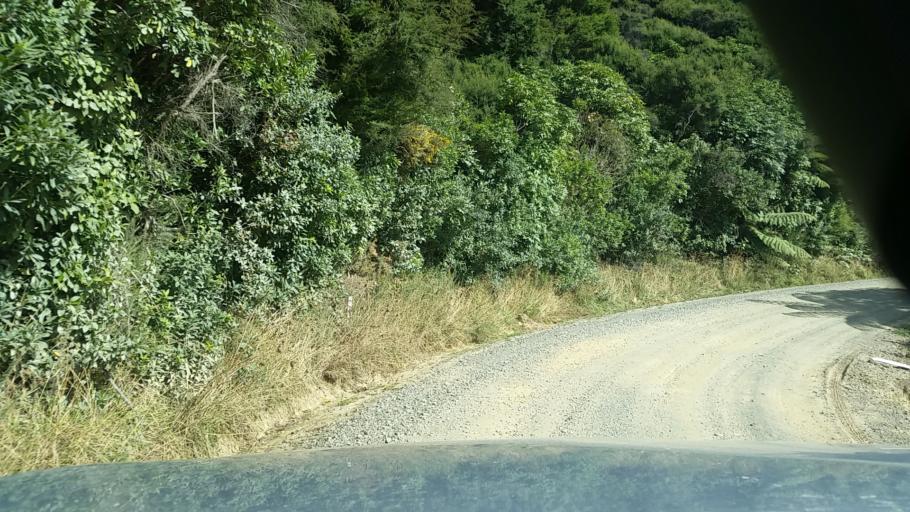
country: NZ
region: Marlborough
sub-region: Marlborough District
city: Picton
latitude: -41.2914
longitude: 174.1295
